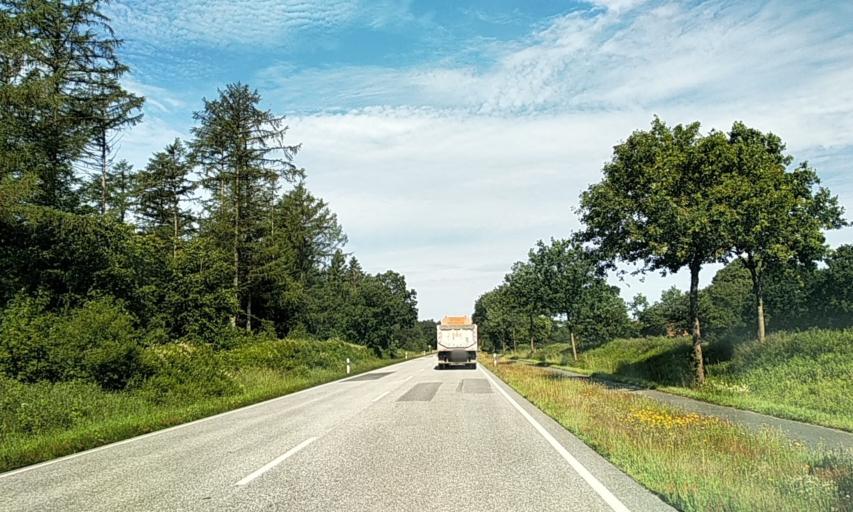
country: DE
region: Schleswig-Holstein
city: Lohe-Fohrden
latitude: 54.3512
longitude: 9.5685
